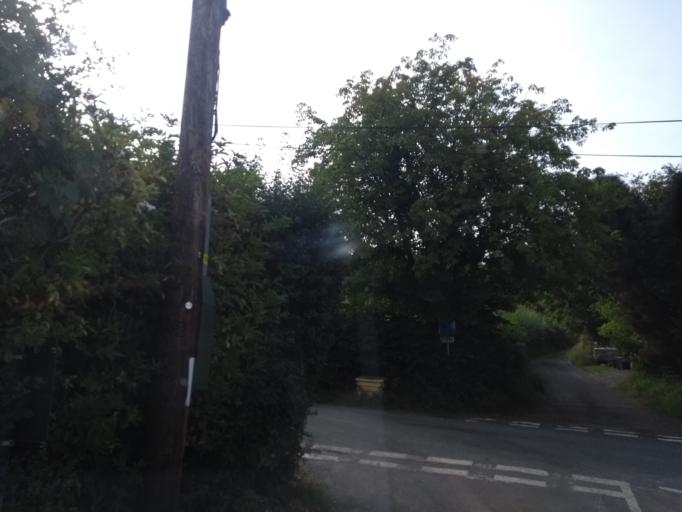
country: GB
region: England
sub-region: Somerset
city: Chard
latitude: 50.8815
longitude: -3.0425
